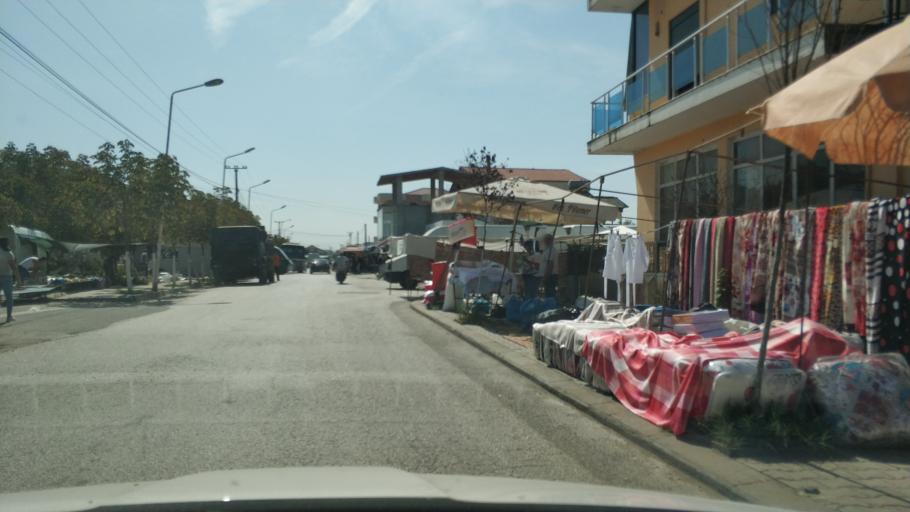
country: AL
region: Fier
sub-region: Rrethi i Lushnjes
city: Divjake
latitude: 40.9941
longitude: 19.5332
